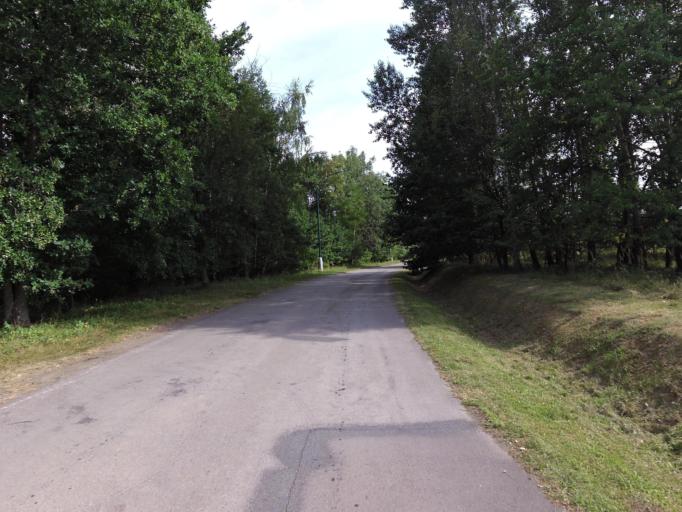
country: CZ
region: Central Bohemia
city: Kamenny Privoz
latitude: 49.8538
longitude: 14.5465
